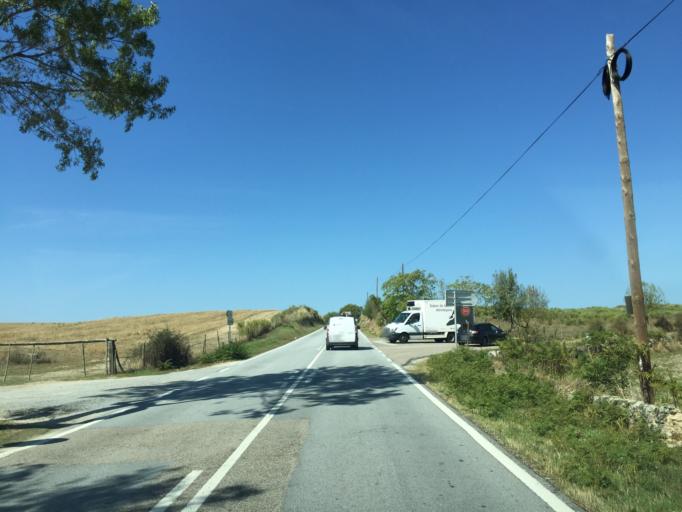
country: PT
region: Portalegre
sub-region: Castelo de Vide
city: Castelo de Vide
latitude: 39.4324
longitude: -7.5054
